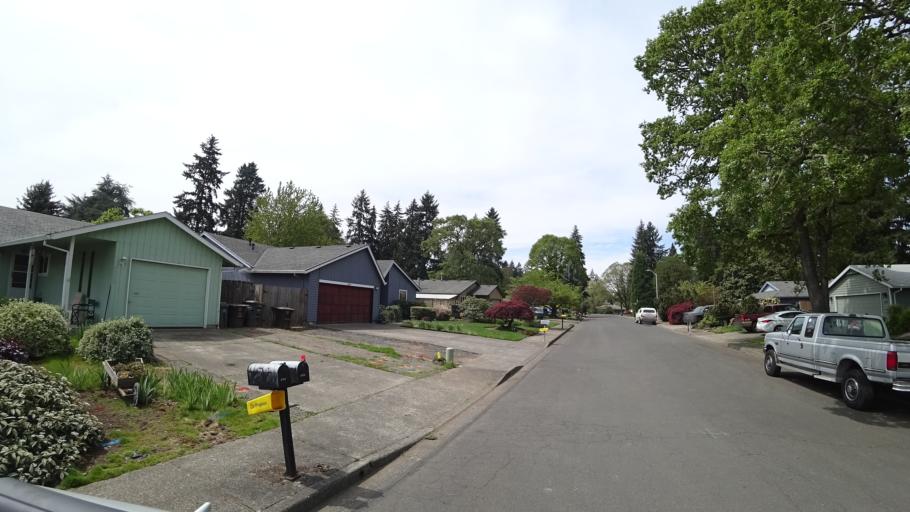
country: US
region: Oregon
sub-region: Washington County
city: Hillsboro
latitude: 45.5138
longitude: -122.9392
